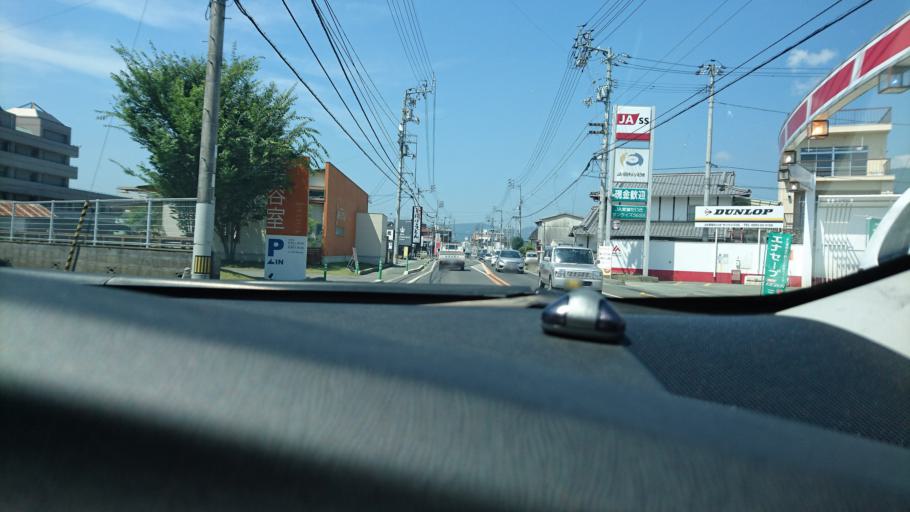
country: JP
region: Ehime
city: Ozu
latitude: 33.5222
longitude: 132.5556
